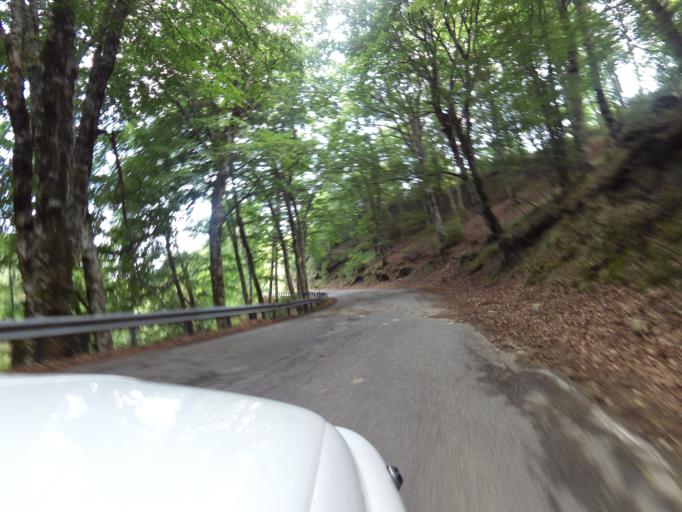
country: IT
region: Calabria
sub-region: Provincia di Vibo-Valentia
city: Nardodipace
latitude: 38.4831
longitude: 16.3788
